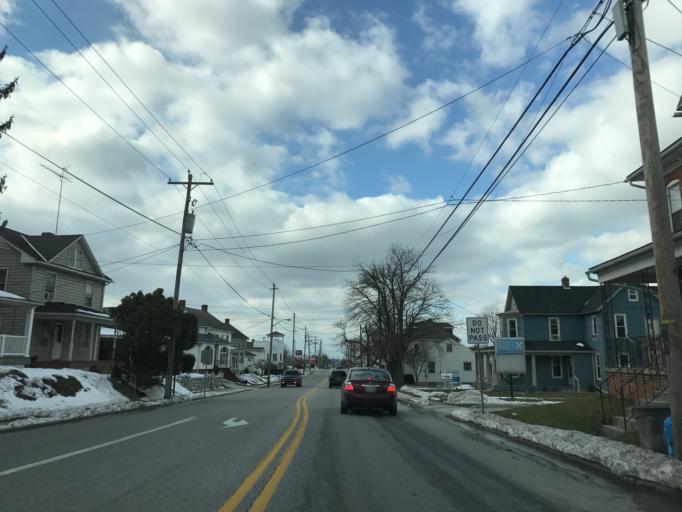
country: US
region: Pennsylvania
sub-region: York County
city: Parkville
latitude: 39.7844
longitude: -76.9657
